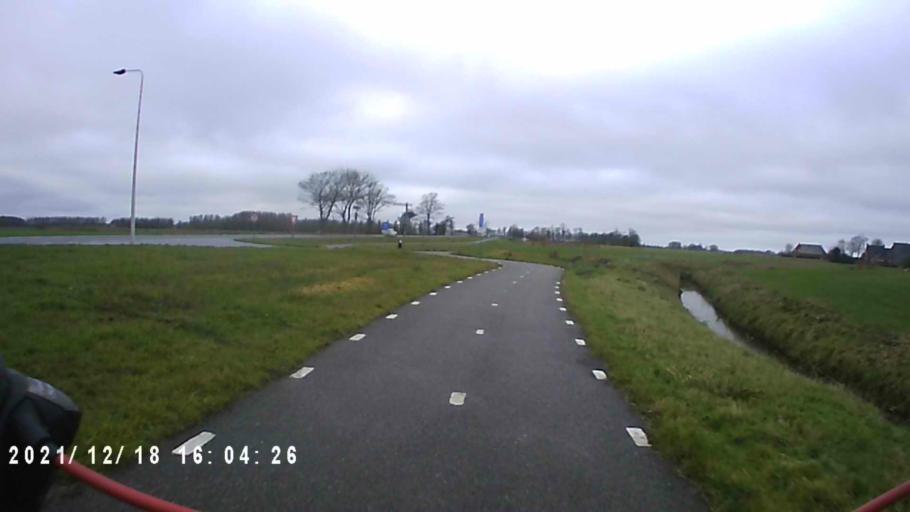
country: NL
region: Friesland
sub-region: Gemeente Dongeradeel
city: Anjum
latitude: 53.3519
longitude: 6.0778
